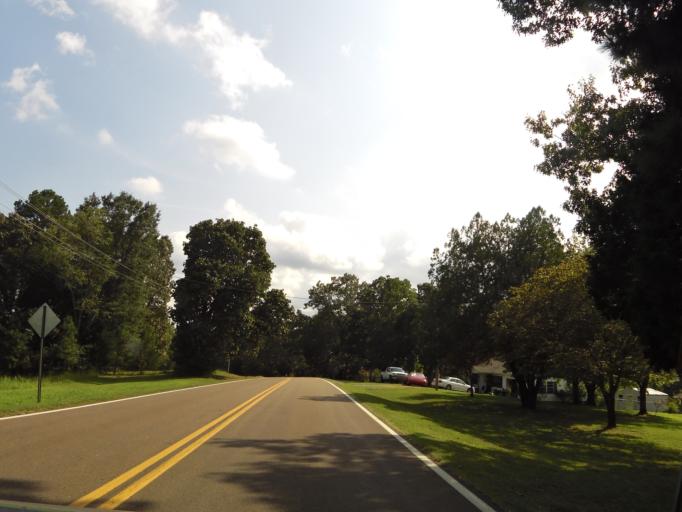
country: US
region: Tennessee
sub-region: McNairy County
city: Adamsville
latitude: 35.0921
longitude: -88.3815
